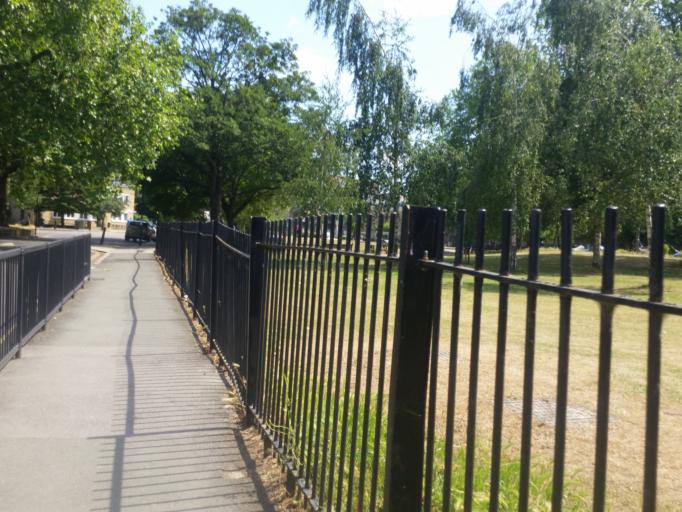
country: GB
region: England
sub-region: Greater London
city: Bethnal Green
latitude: 51.5400
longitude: -0.0753
